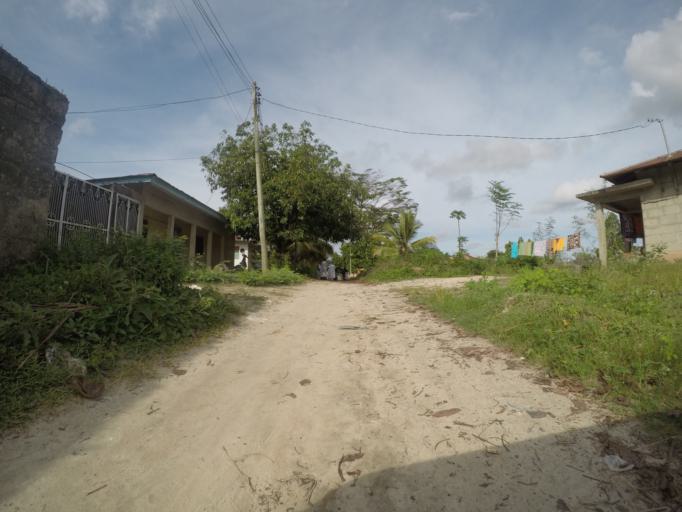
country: TZ
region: Pemba South
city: Chake Chake
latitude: -5.2240
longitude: 39.7785
